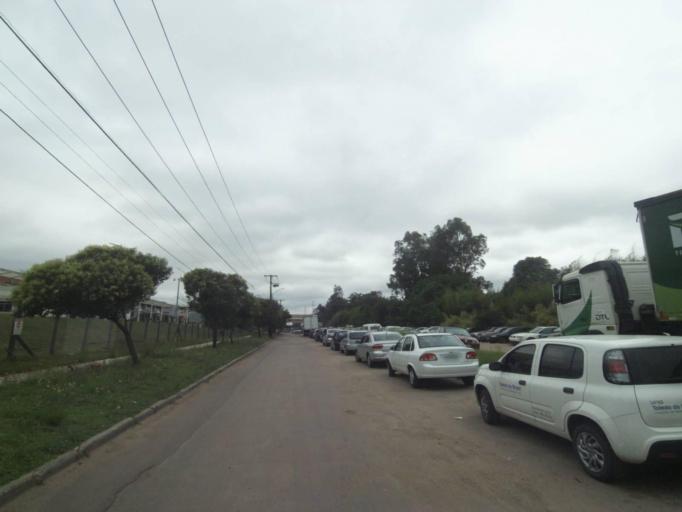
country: BR
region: Parana
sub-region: Araucaria
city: Araucaria
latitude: -25.5419
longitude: -49.3166
